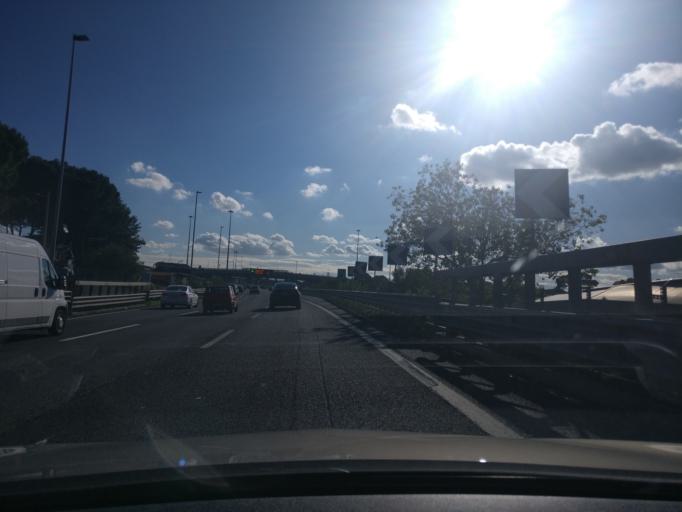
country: IT
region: Latium
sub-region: Citta metropolitana di Roma Capitale
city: Ciampino
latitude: 41.8263
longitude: 12.5810
